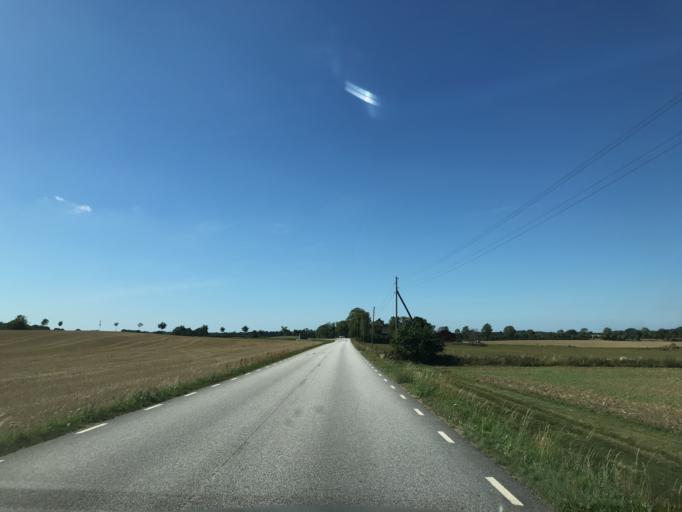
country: SE
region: Skane
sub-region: Tomelilla Kommun
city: Tomelilla
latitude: 55.6454
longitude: 13.9778
